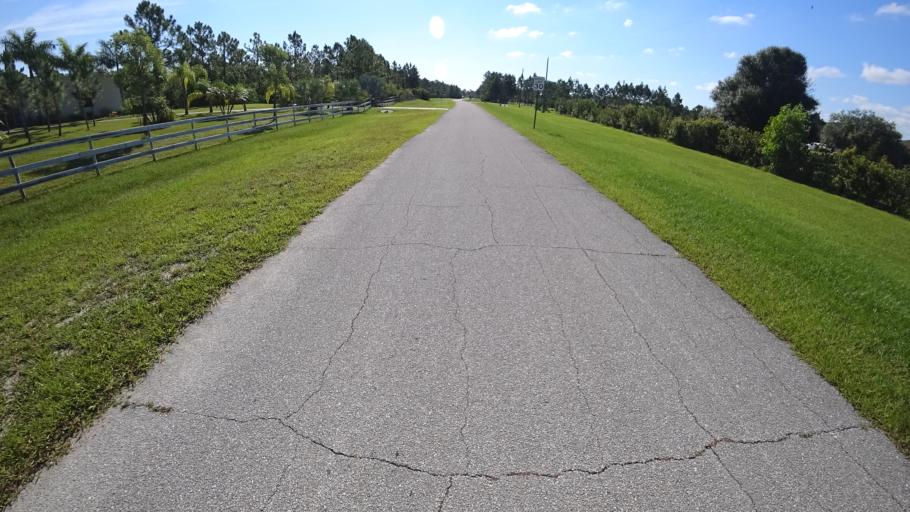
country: US
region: Florida
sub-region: Sarasota County
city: The Meadows
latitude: 27.4244
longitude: -82.3486
